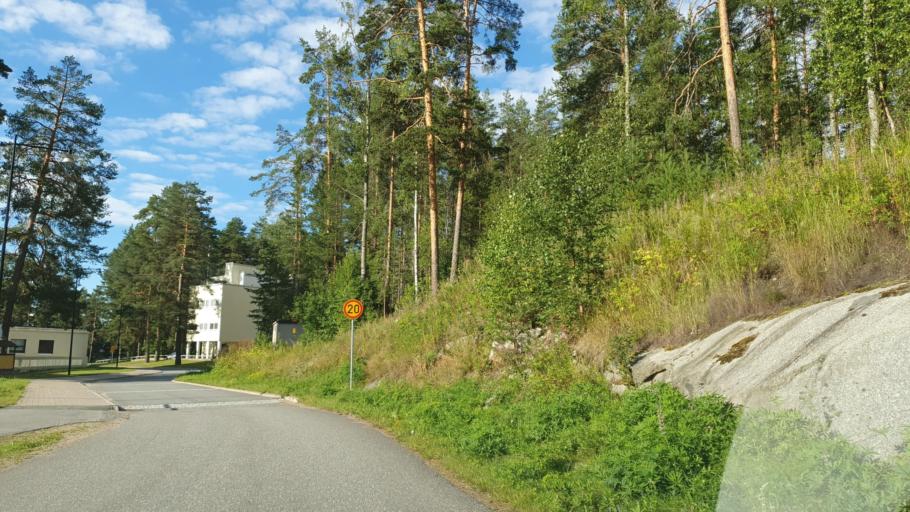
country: FI
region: Central Finland
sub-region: Jyvaeskylae
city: Saeynaetsalo
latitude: 62.1594
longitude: 25.7648
